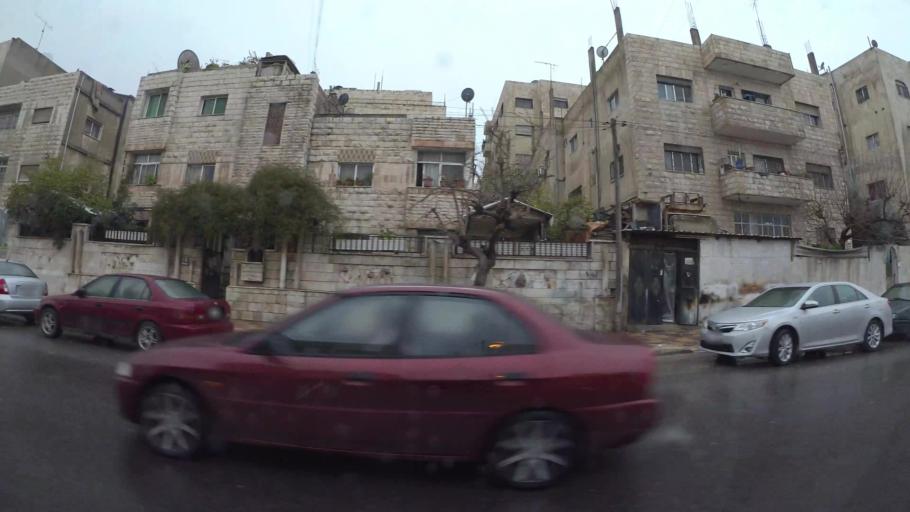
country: JO
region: Amman
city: Amman
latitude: 31.9734
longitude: 35.9207
